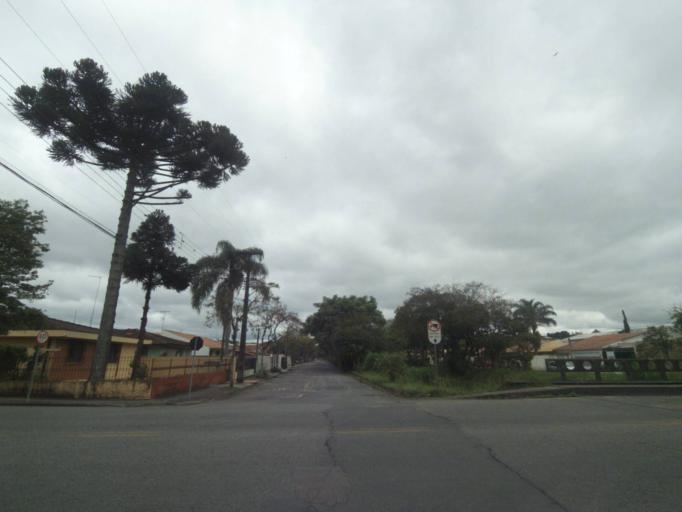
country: BR
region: Parana
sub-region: Pinhais
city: Pinhais
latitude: -25.3989
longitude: -49.2198
